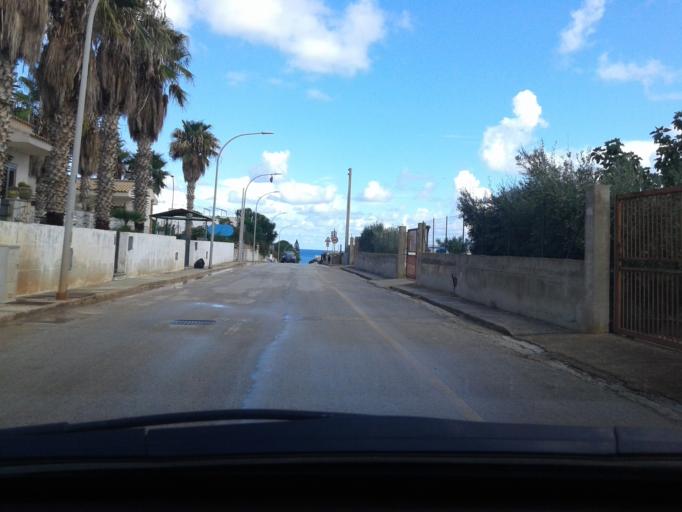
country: IT
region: Sicily
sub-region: Trapani
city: San Vito Lo Capo
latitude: 38.1707
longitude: 12.7422
